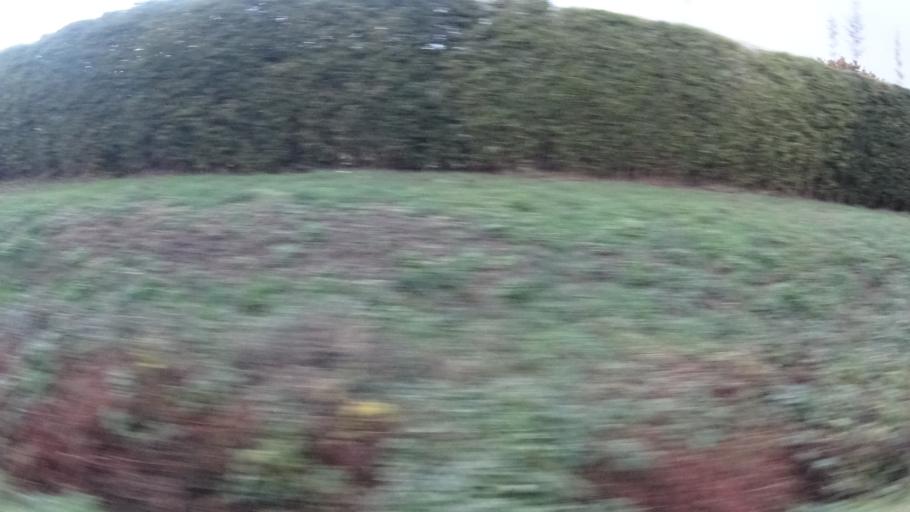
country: FR
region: Brittany
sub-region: Departement d'Ille-et-Vilaine
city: Sainte-Marie
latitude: 47.6820
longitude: -1.9947
